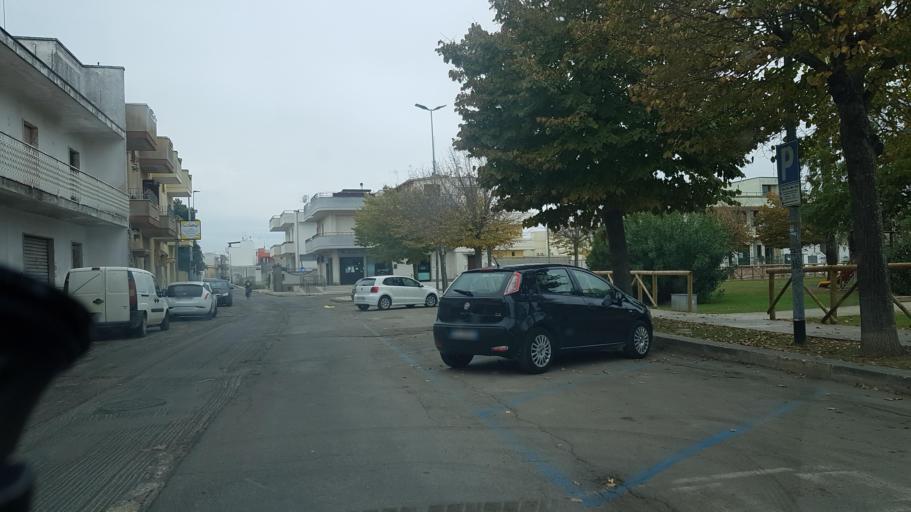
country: IT
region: Apulia
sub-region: Provincia di Lecce
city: Leverano
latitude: 40.2879
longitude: 17.9956
